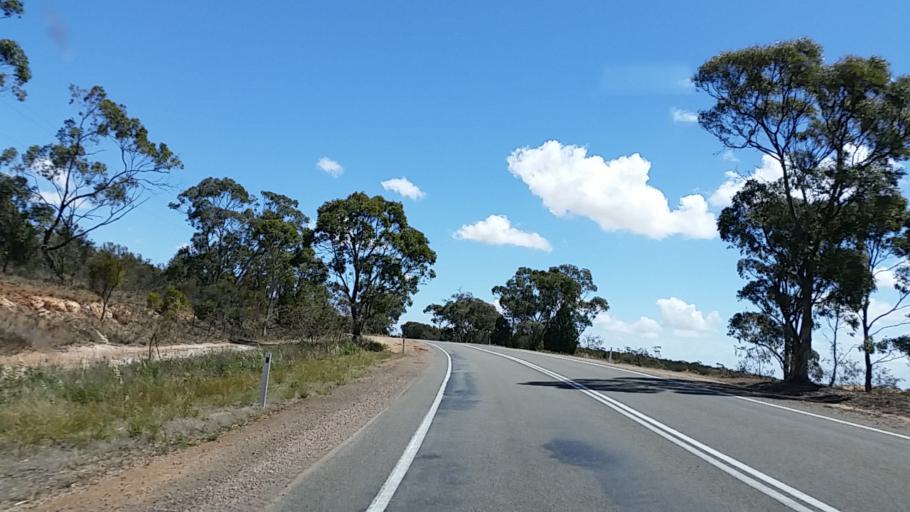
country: AU
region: South Australia
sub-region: Port Pirie City and Dists
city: Crystal Brook
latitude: -33.2837
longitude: 138.2638
